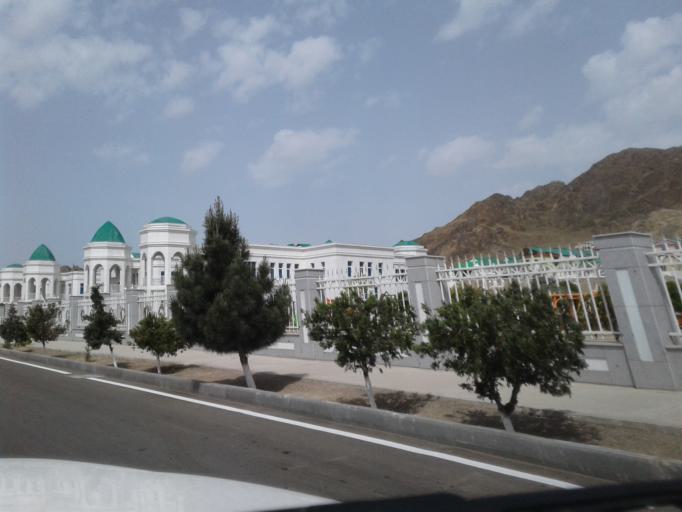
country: TM
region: Balkan
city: Turkmenbasy
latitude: 39.9906
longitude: 52.9837
